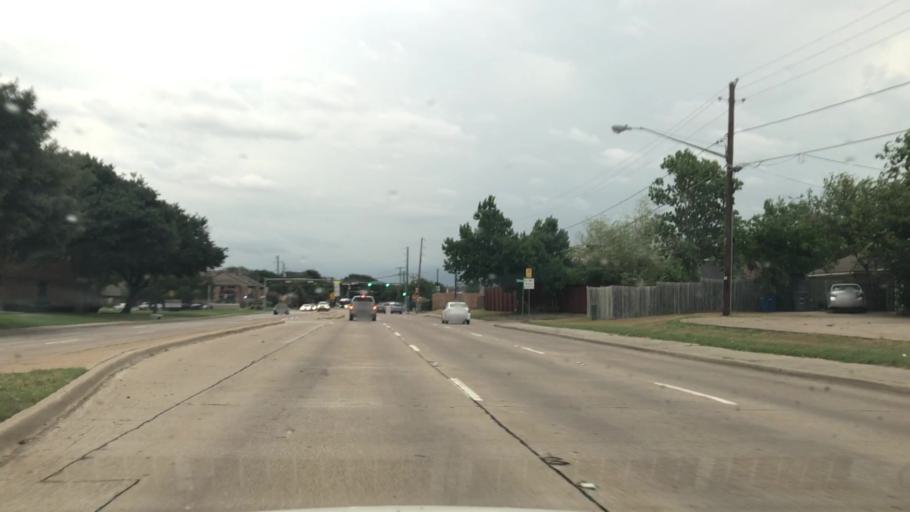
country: US
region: Texas
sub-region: Dallas County
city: Carrollton
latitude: 32.9968
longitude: -96.8703
